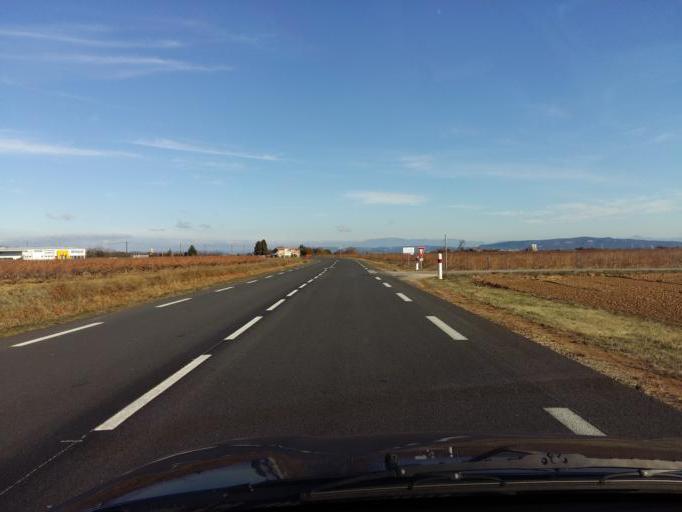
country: FR
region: Rhone-Alpes
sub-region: Departement de l'Ardeche
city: Saint-Just-d'Ardeche
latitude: 44.3149
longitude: 4.6184
